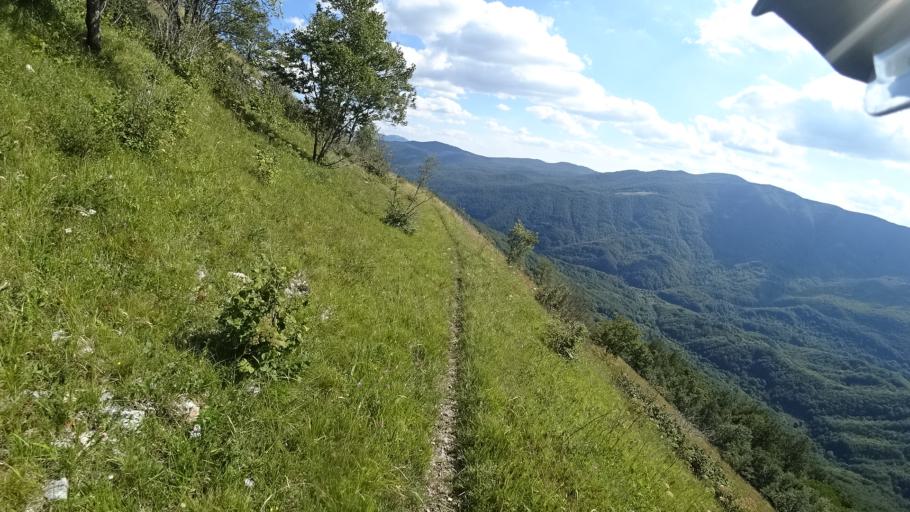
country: HR
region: Zadarska
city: Gracac
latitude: 44.3816
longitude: 16.0465
